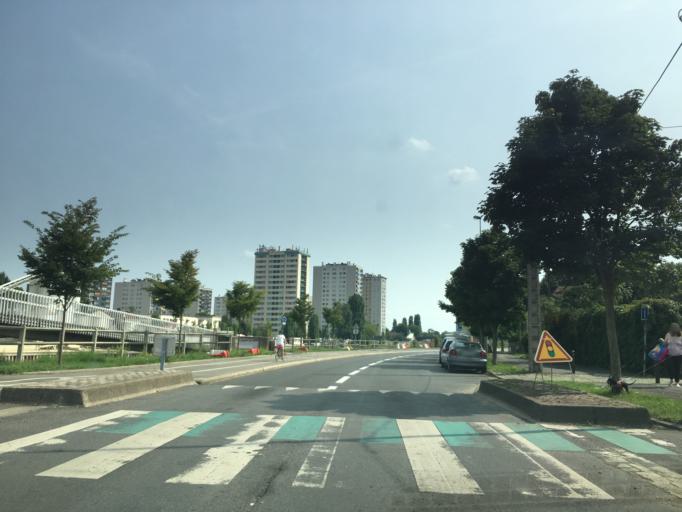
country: FR
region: Ile-de-France
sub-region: Departement du Val-de-Marne
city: Creteil
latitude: 48.8044
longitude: 2.4674
